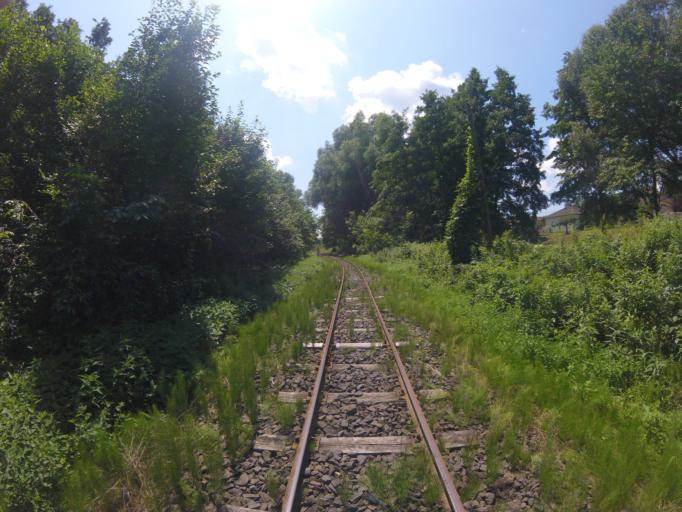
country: HU
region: Zala
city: Letenye
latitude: 46.5199
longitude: 16.7287
